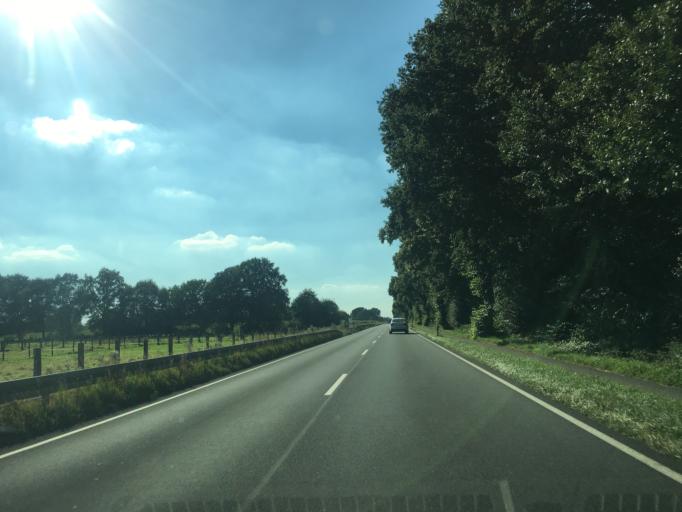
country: DE
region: North Rhine-Westphalia
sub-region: Regierungsbezirk Munster
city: Warendorf
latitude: 51.9553
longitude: 7.9607
